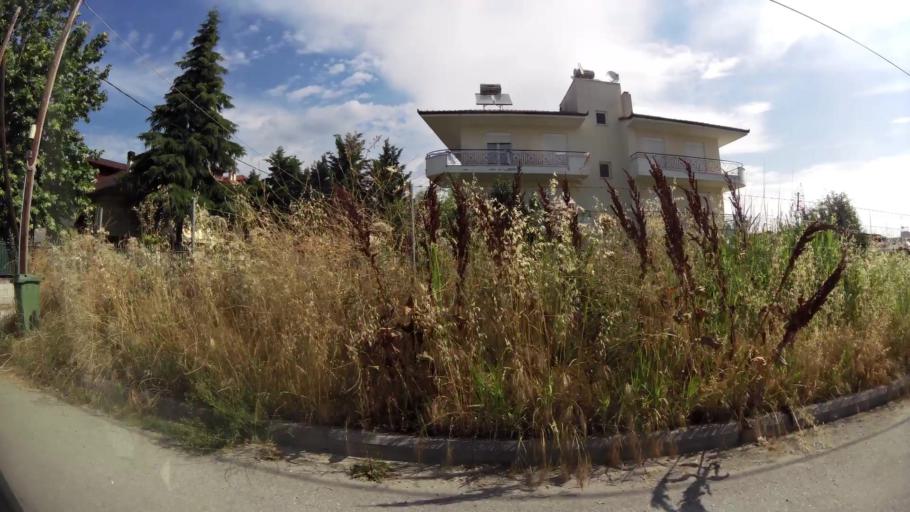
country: GR
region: Central Macedonia
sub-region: Nomos Pierias
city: Katerini
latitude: 40.2813
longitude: 22.4969
